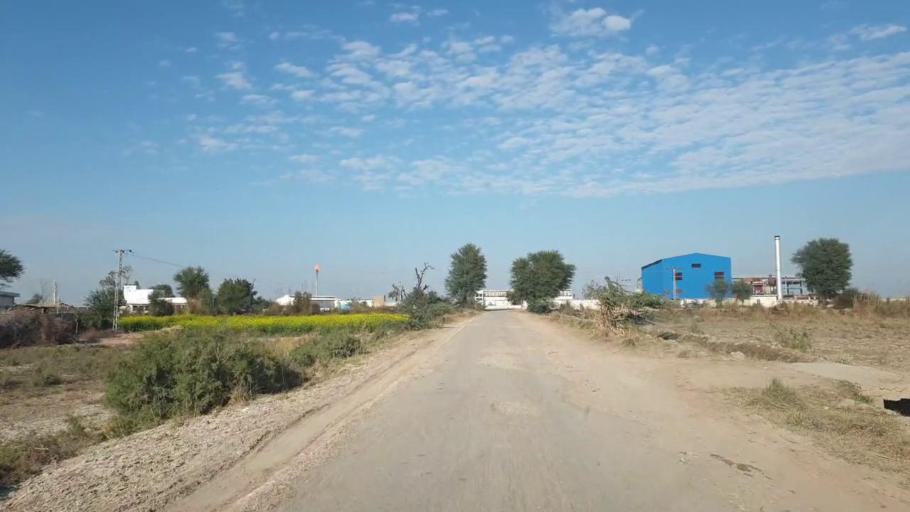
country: PK
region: Sindh
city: Sanghar
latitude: 26.0880
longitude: 68.8779
